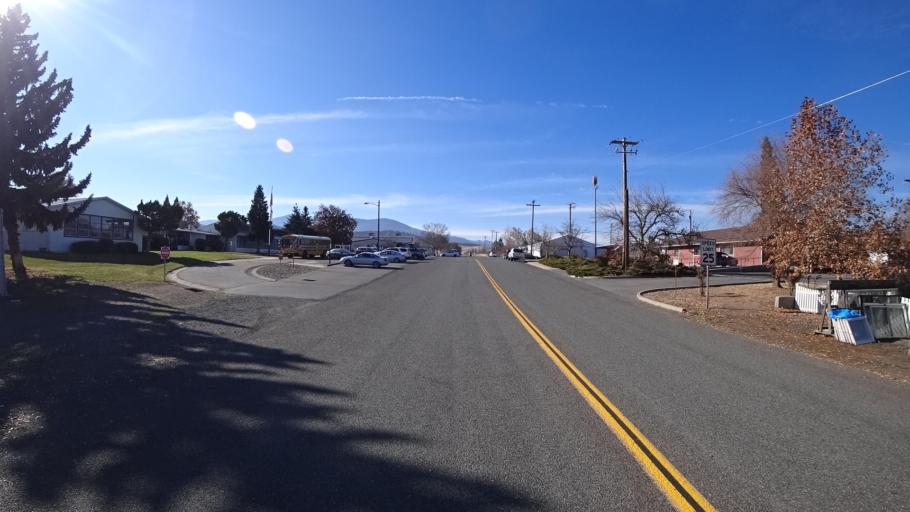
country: US
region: California
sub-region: Siskiyou County
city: Montague
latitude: 41.6456
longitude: -122.5240
